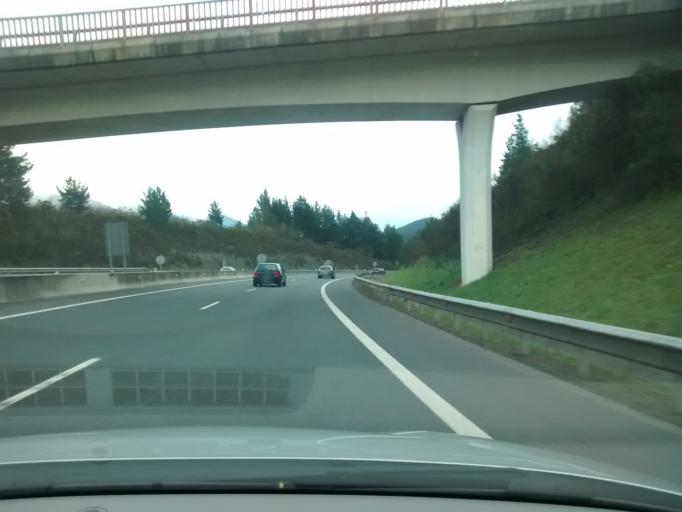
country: ES
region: Basque Country
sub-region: Bizkaia
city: Guenes
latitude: 43.2085
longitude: -3.0989
